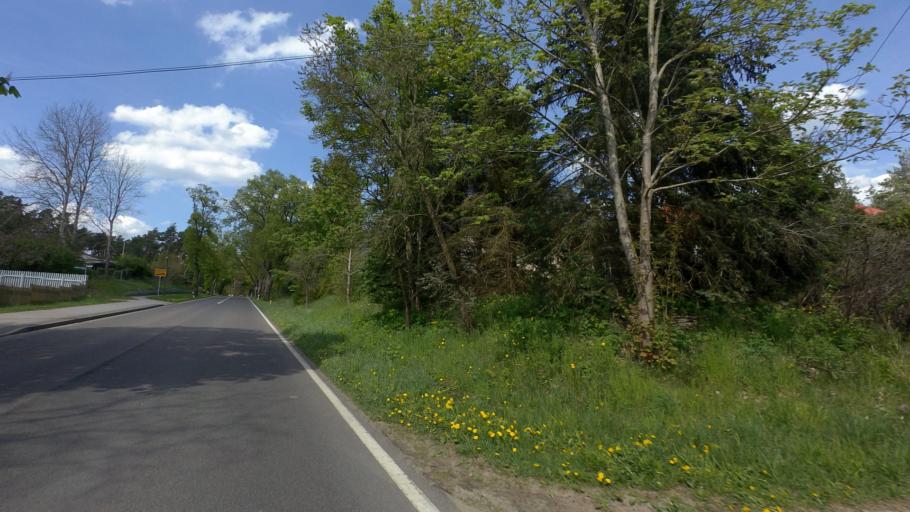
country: DE
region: Brandenburg
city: Milmersdorf
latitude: 53.0760
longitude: 13.6223
